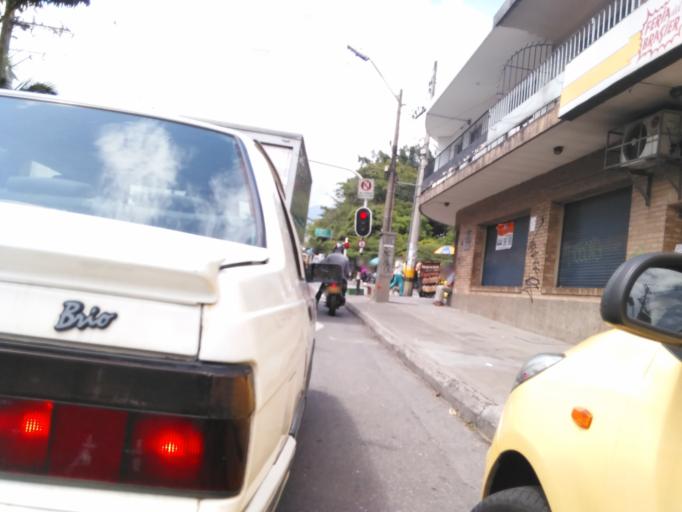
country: CO
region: Antioquia
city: Medellin
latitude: 6.2322
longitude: -75.5959
